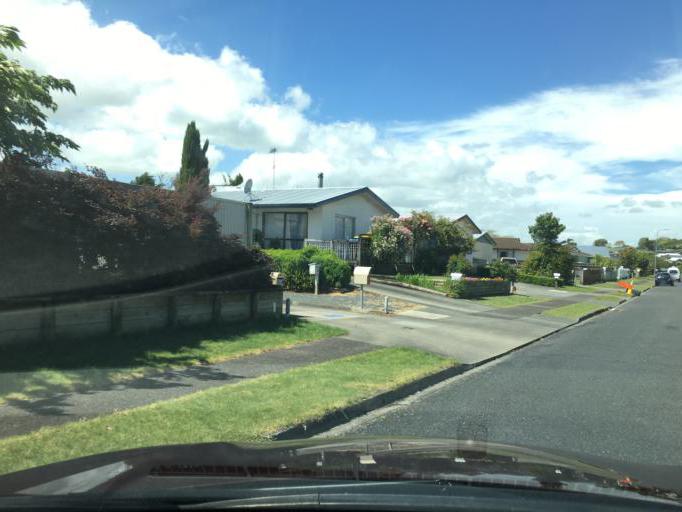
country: NZ
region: Waikato
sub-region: Waipa District
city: Cambridge
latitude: -38.0051
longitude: 175.3369
